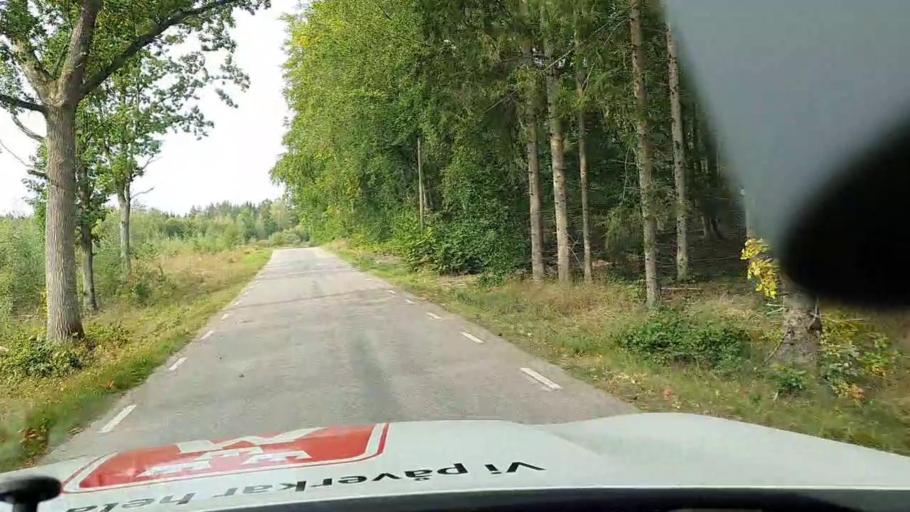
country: SE
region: Soedermanland
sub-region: Nykopings Kommun
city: Svalsta
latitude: 58.8313
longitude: 16.8787
